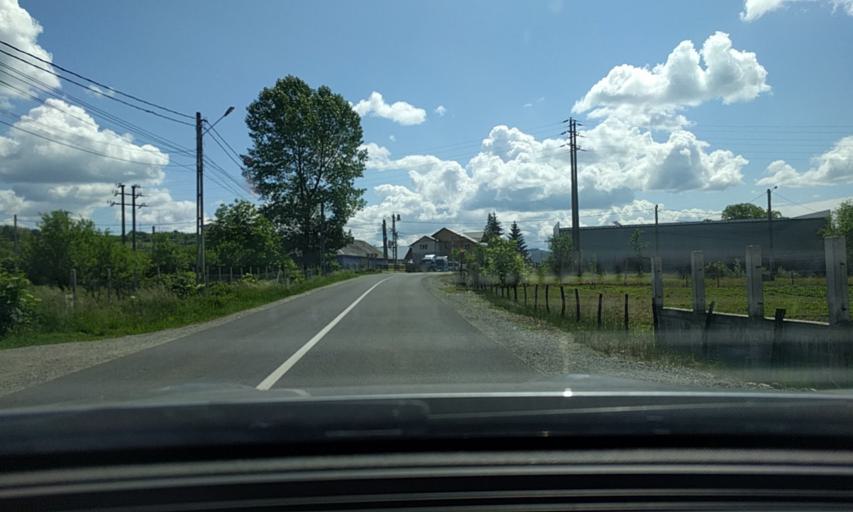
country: RO
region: Bistrita-Nasaud
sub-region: Oras Nasaud
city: Nasaud
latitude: 47.2971
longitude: 24.3791
